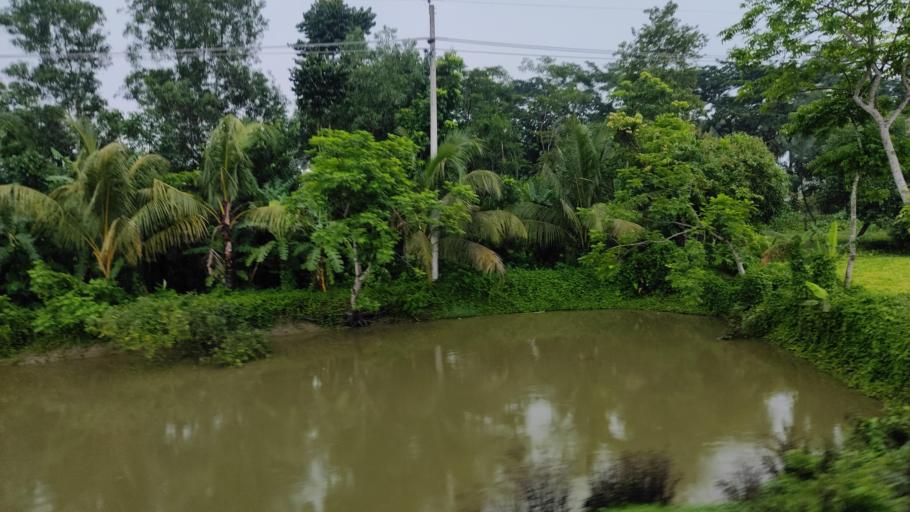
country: BD
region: Barisal
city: Bhandaria
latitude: 22.3182
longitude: 90.3257
